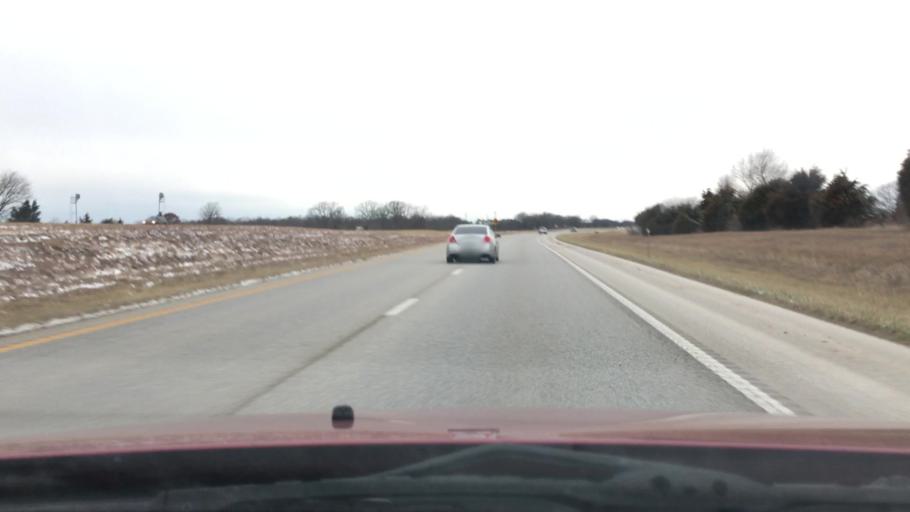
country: US
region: Missouri
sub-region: Webster County
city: Seymour
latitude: 37.1693
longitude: -92.8225
